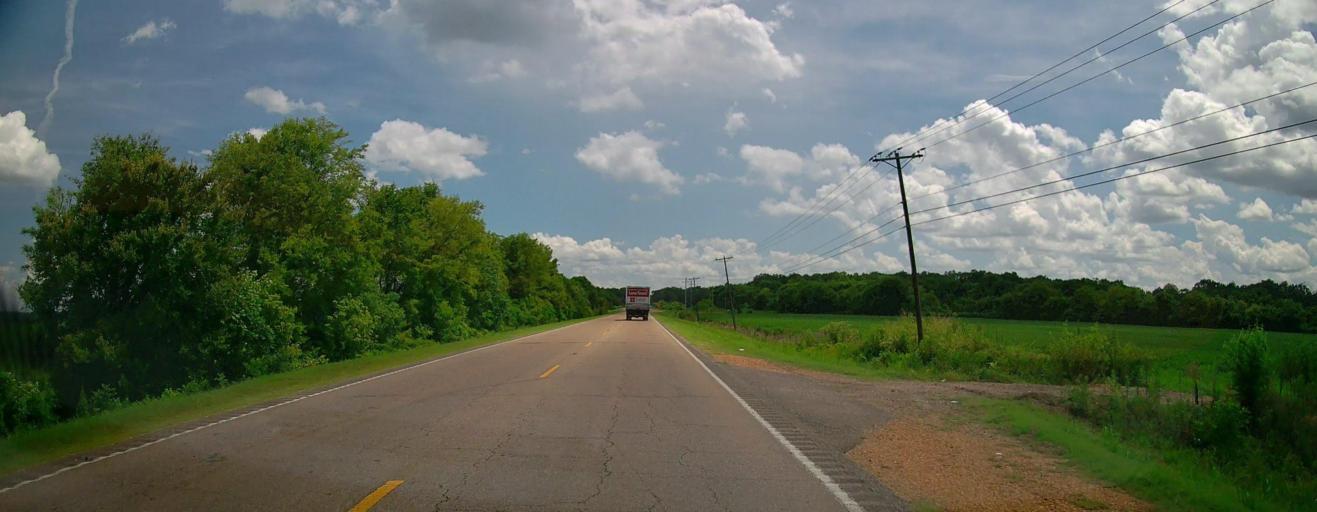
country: US
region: Mississippi
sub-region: Lee County
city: Shannon
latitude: 34.1433
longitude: -88.7194
